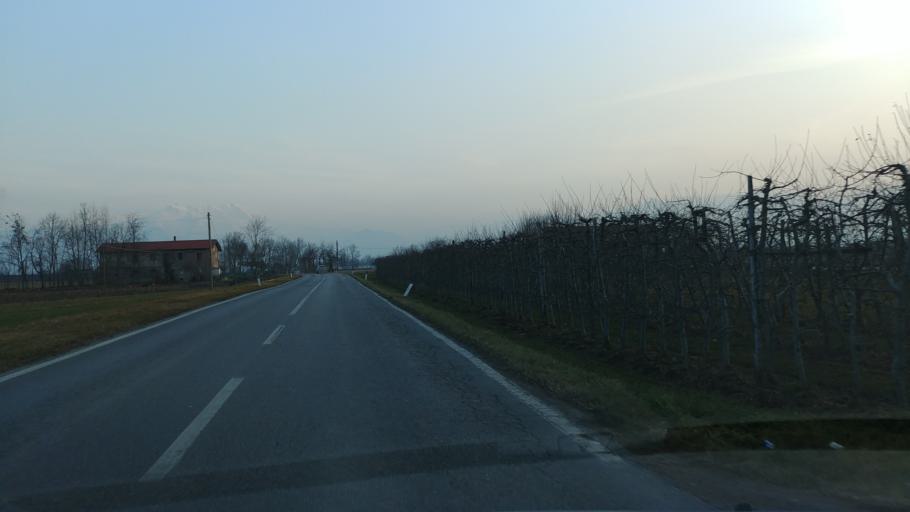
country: IT
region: Piedmont
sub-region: Provincia di Cuneo
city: Roata Rossi
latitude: 44.4218
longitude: 7.5074
